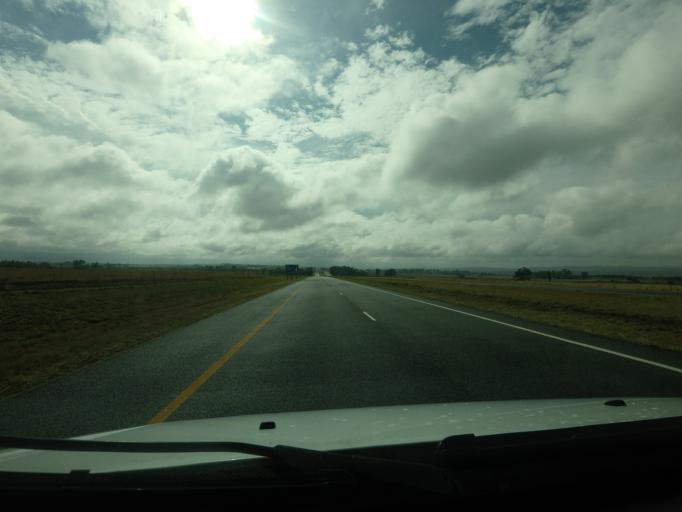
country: ZA
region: Gauteng
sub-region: City of Tshwane Metropolitan Municipality
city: Bronkhorstspruit
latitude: -25.7988
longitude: 28.5997
